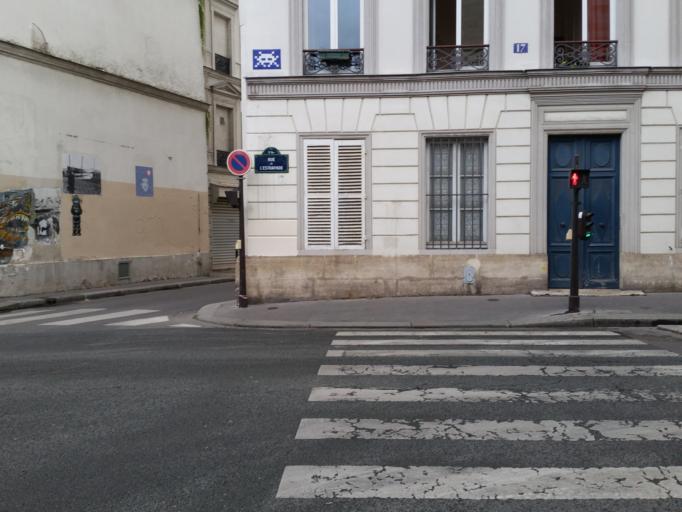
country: FR
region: Ile-de-France
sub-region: Paris
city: Paris
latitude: 48.8449
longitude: 2.3465
